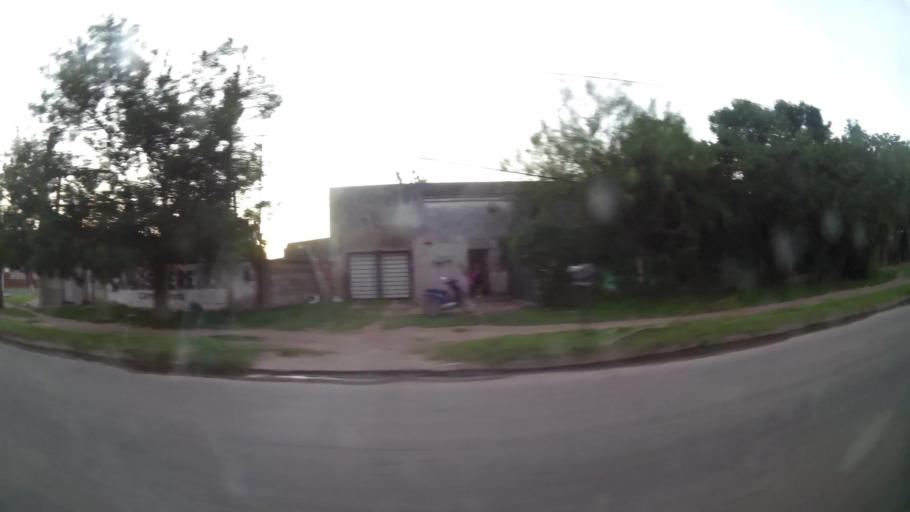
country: AR
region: Santa Fe
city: Santa Fe de la Vera Cruz
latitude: -31.6069
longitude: -60.7131
